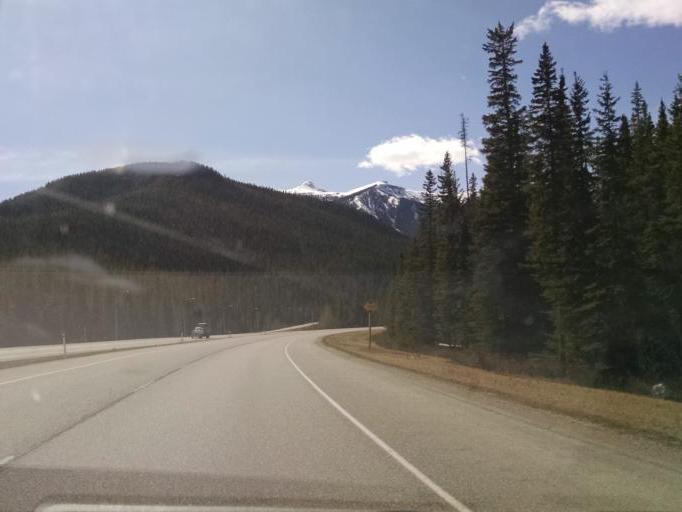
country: CA
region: Alberta
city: Banff
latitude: 51.1579
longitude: -115.6809
